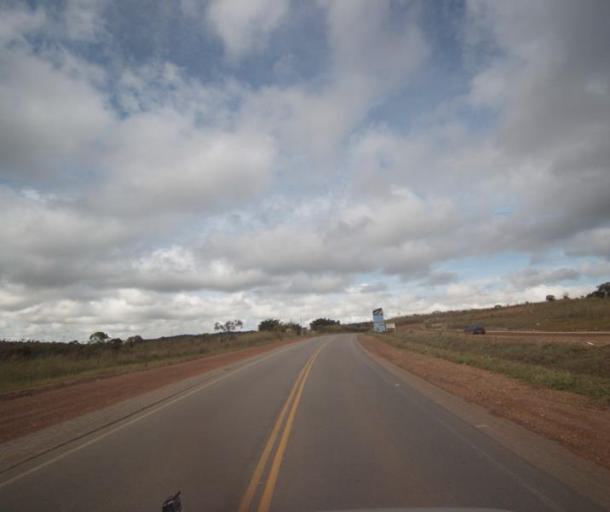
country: BR
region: Goias
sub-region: Pirenopolis
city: Pirenopolis
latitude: -15.8261
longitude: -48.7785
